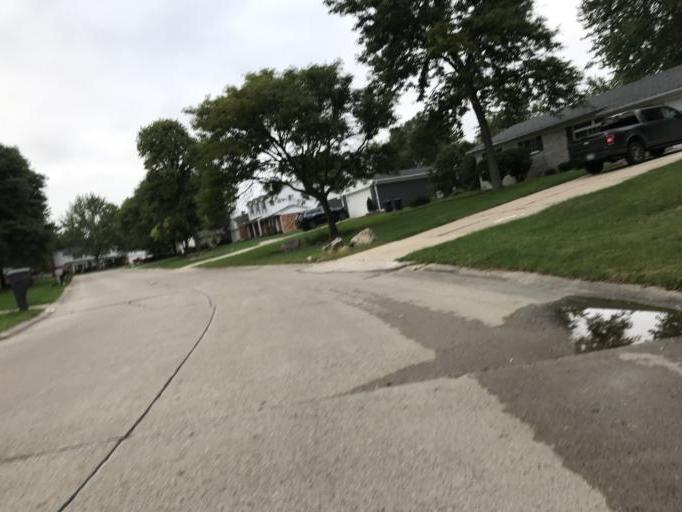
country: US
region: Michigan
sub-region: Oakland County
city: Franklin
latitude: 42.4832
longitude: -83.3293
